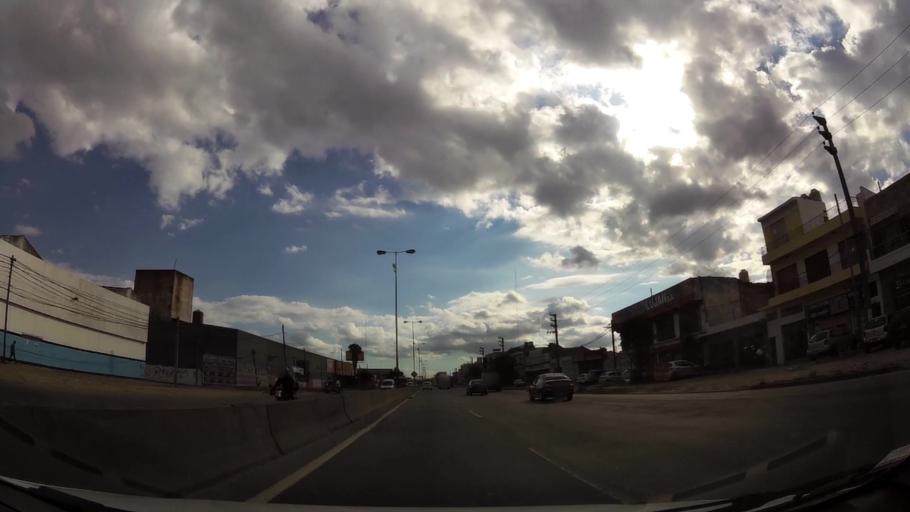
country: AR
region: Buenos Aires
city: San Justo
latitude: -34.6890
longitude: -58.5667
